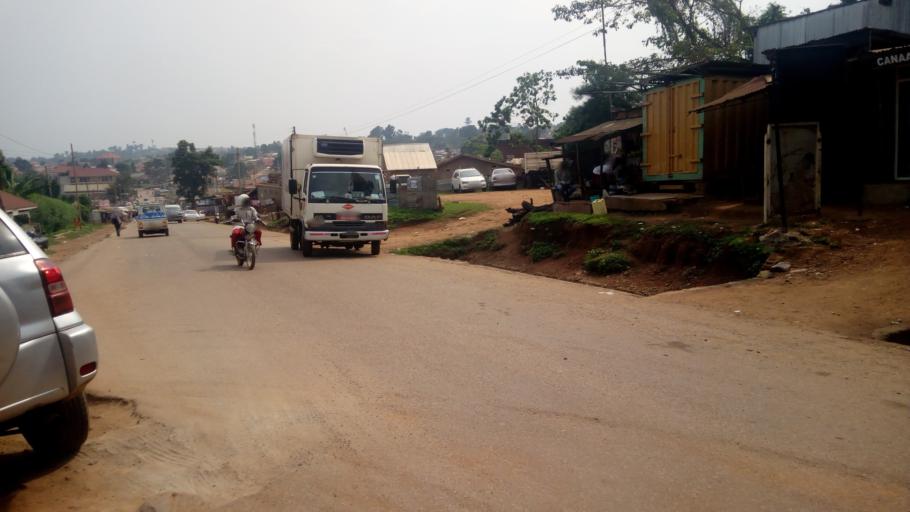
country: UG
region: Central Region
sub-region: Wakiso District
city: Kireka
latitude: 0.3072
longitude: 32.6552
